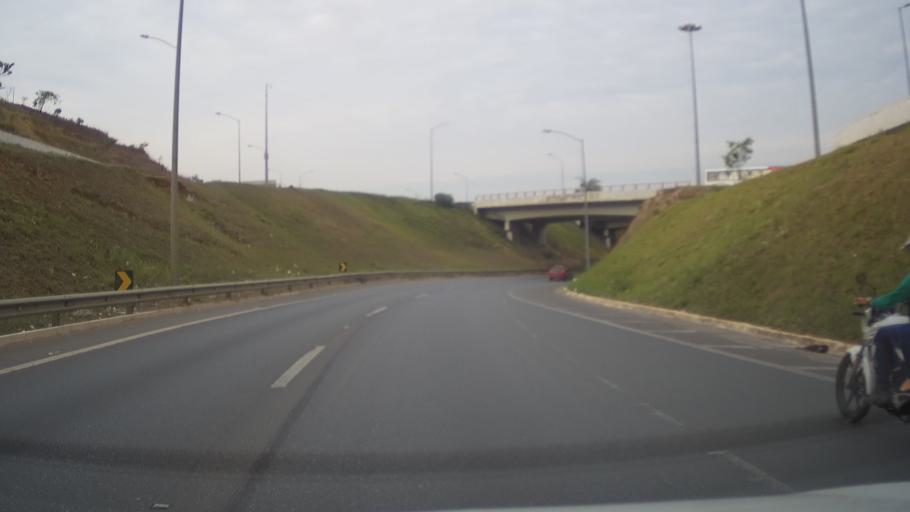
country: BR
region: Minas Gerais
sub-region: Vespasiano
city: Vespasiano
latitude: -19.7595
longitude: -43.9480
